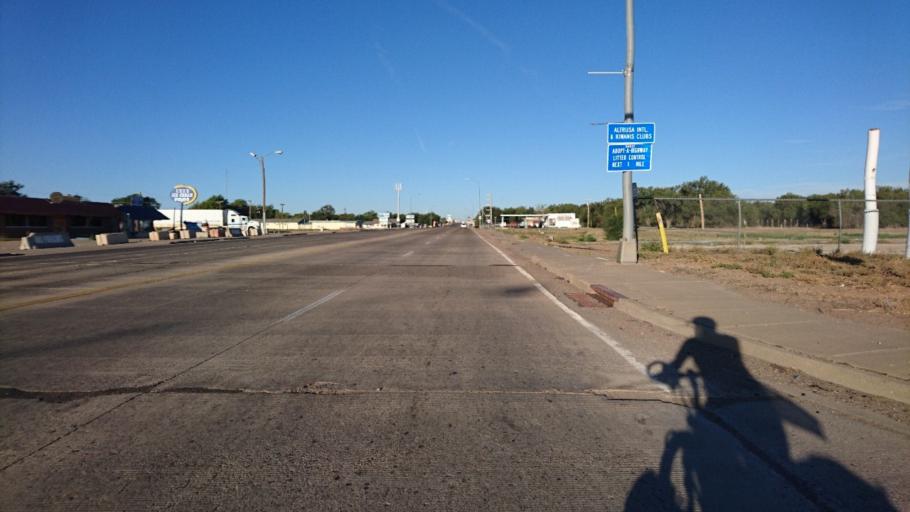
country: US
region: New Mexico
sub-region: Quay County
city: Tucumcari
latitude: 35.1719
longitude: -103.7025
